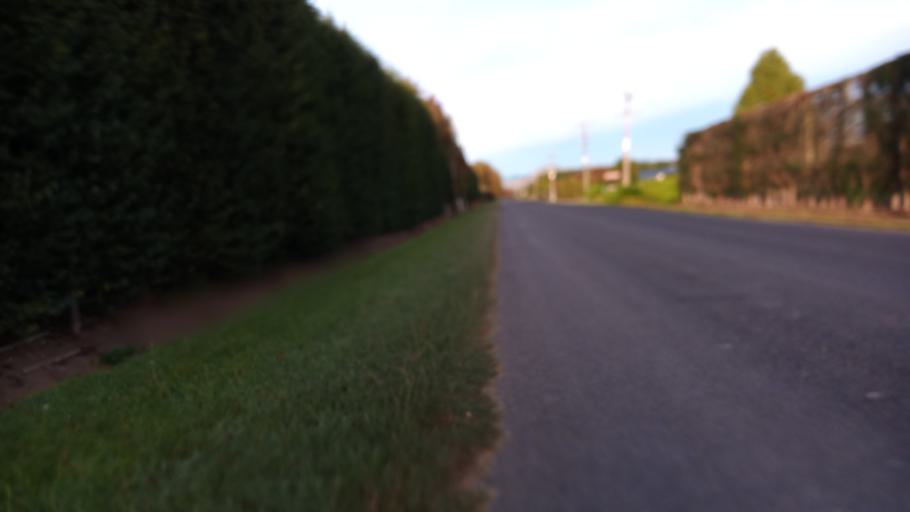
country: NZ
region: Gisborne
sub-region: Gisborne District
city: Gisborne
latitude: -38.6526
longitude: 177.9402
